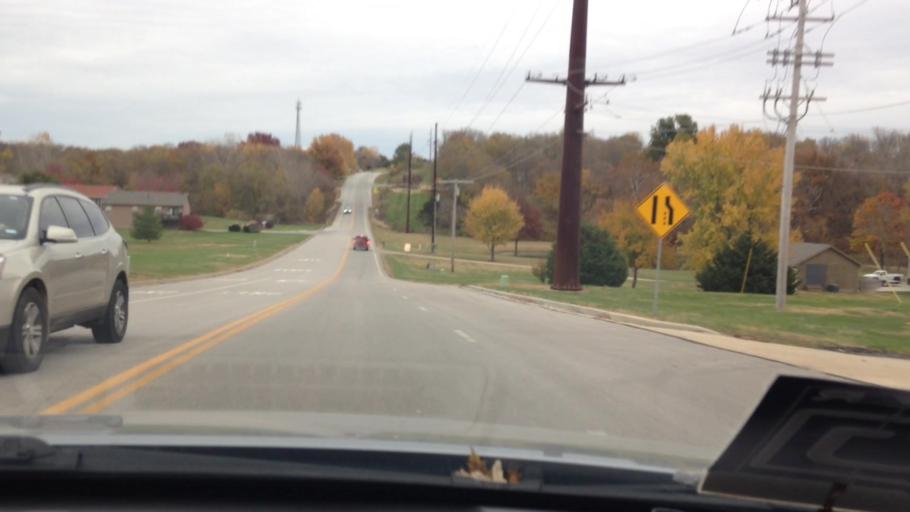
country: US
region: Missouri
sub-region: Platte County
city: Platte City
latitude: 39.3395
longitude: -94.7609
